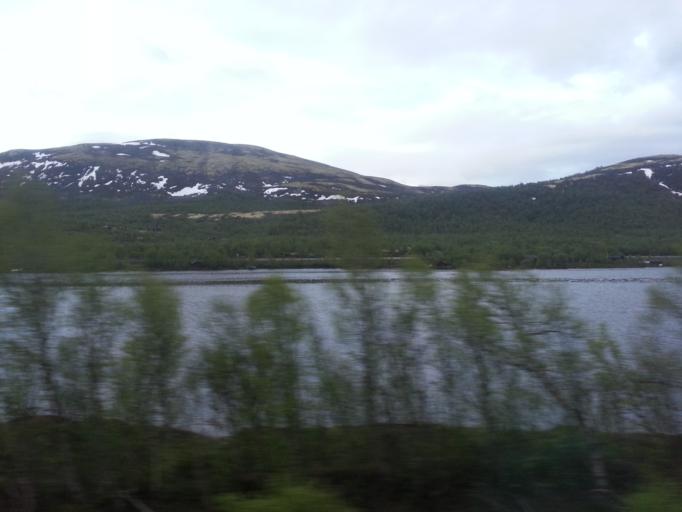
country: NO
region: Oppland
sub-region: Dovre
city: Dovre
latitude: 62.1765
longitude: 9.4203
